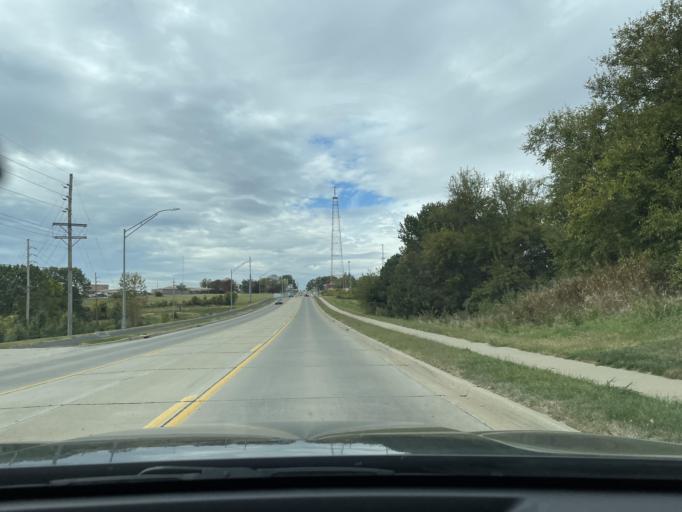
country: US
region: Missouri
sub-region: Buchanan County
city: Saint Joseph
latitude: 39.7698
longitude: -94.7896
